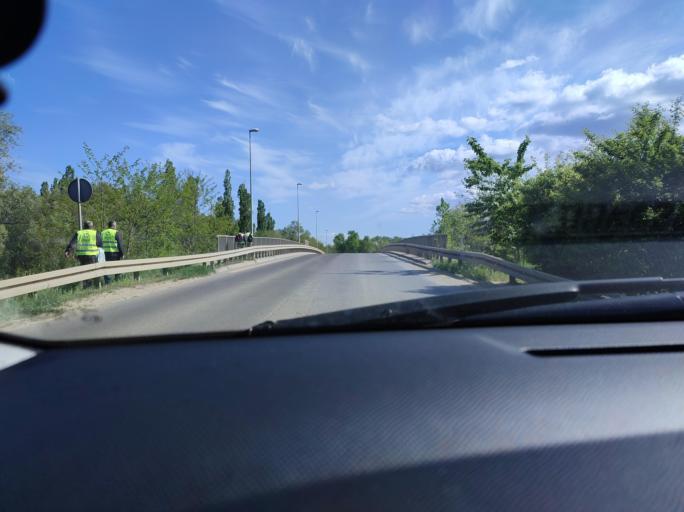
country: PL
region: West Pomeranian Voivodeship
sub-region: Powiat policki
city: Police
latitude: 53.5624
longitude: 14.5260
